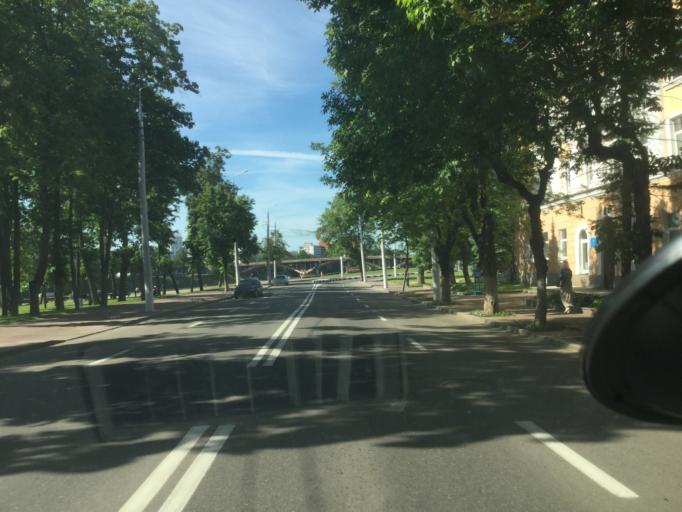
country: BY
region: Vitebsk
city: Vitebsk
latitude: 55.1889
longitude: 30.2008
